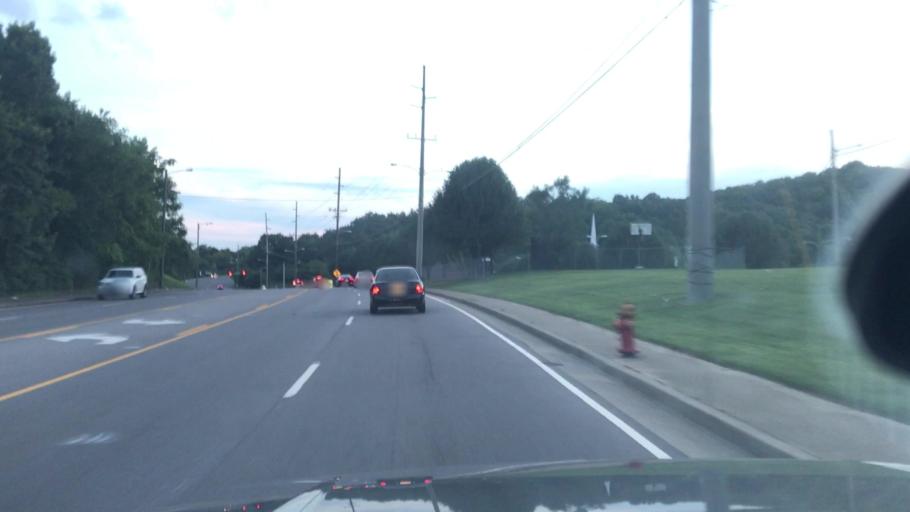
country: US
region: Tennessee
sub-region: Davidson County
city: Nashville
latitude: 36.2040
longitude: -86.8187
